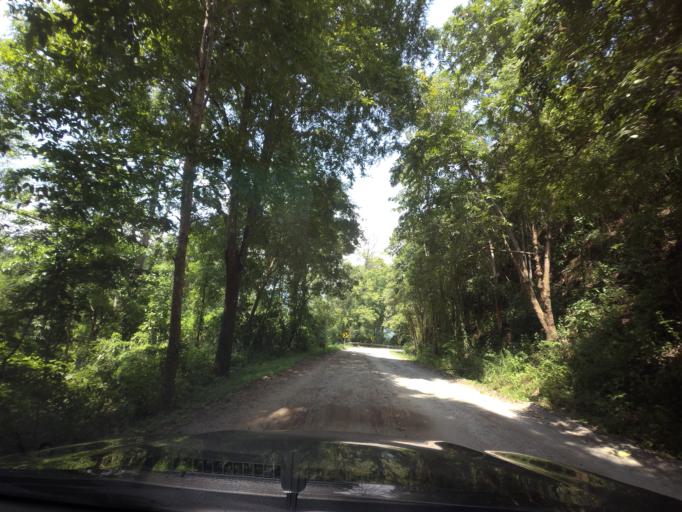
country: TH
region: Loei
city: Na Haeo
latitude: 17.6219
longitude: 100.8997
